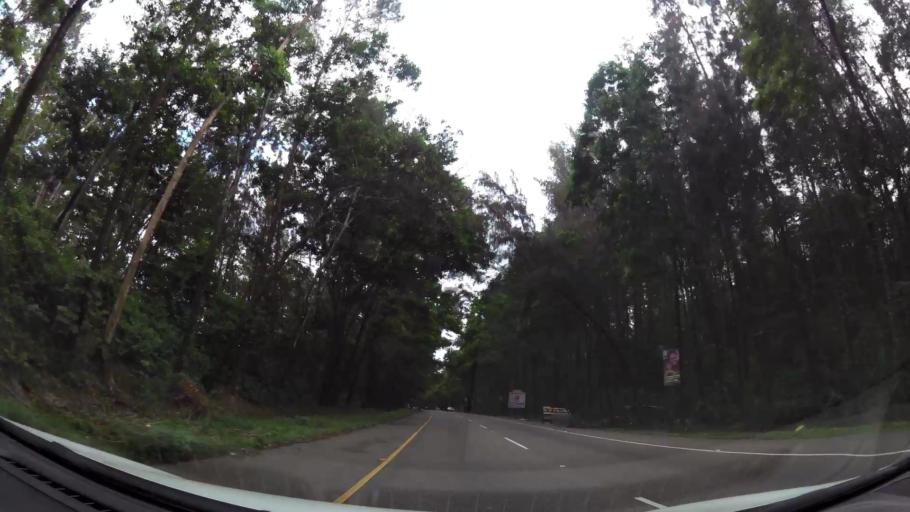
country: DO
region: La Vega
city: Rincon
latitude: 19.1240
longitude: -70.4529
